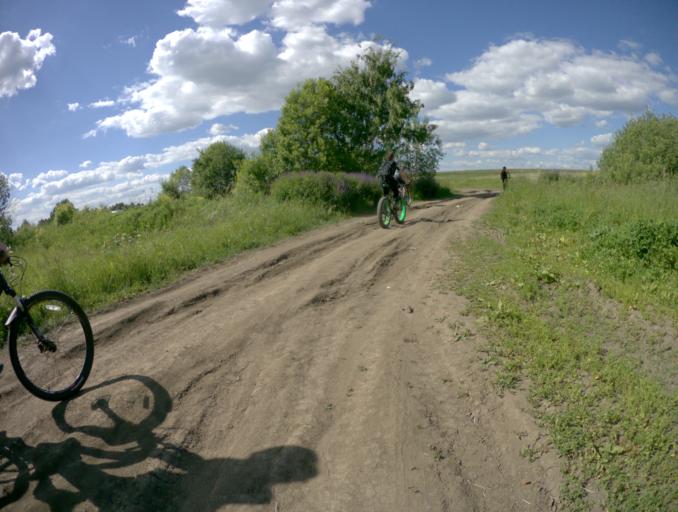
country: RU
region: Vladimir
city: Suzdal'
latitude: 56.3383
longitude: 40.3422
